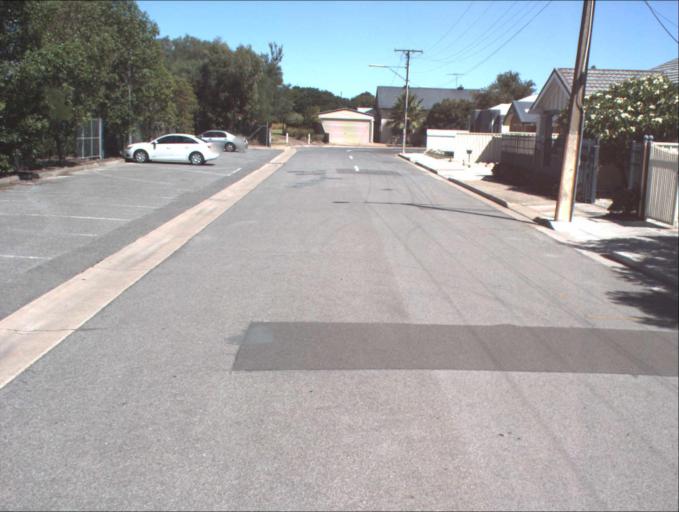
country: AU
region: South Australia
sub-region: Port Adelaide Enfield
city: Birkenhead
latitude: -34.8345
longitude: 138.4917
